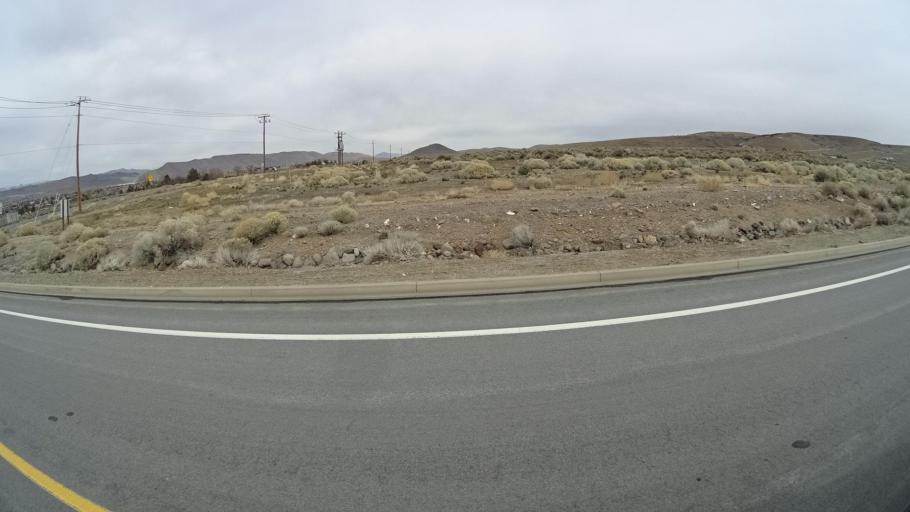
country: US
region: Nevada
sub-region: Washoe County
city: Spanish Springs
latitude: 39.6362
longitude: -119.6725
